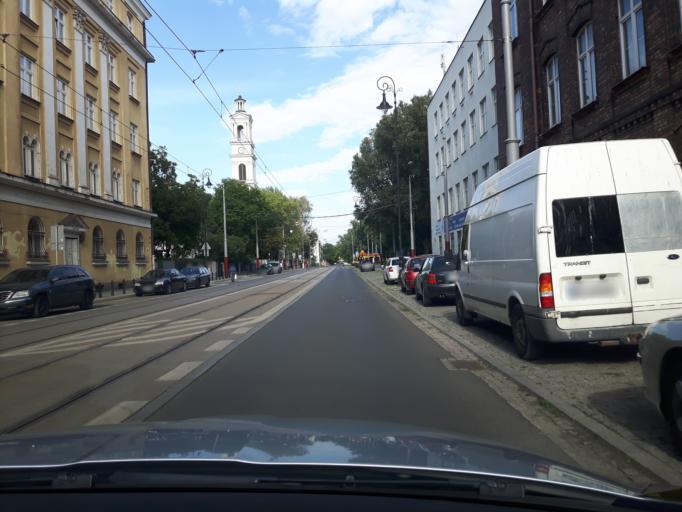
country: PL
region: Masovian Voivodeship
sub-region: Warszawa
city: Praga Polnoc
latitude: 52.2576
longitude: 21.0573
